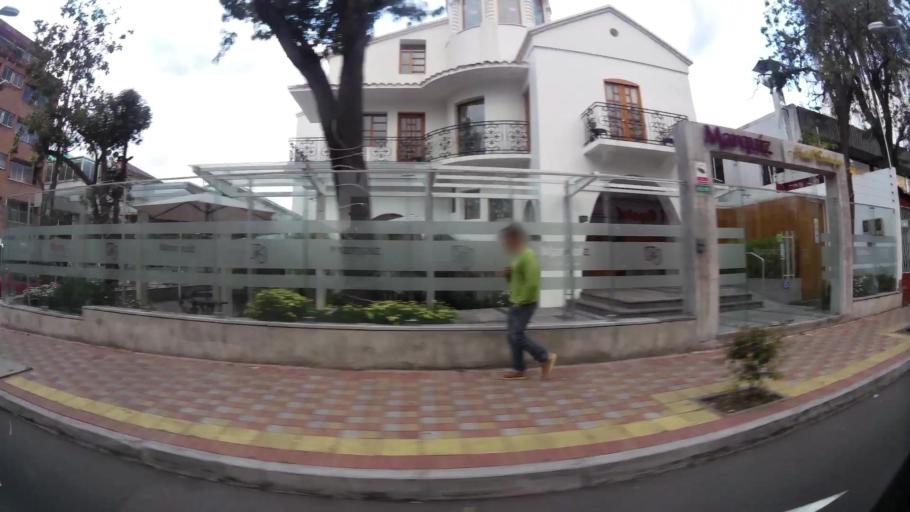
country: EC
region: Pichincha
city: Quito
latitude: -0.2027
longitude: -78.4925
